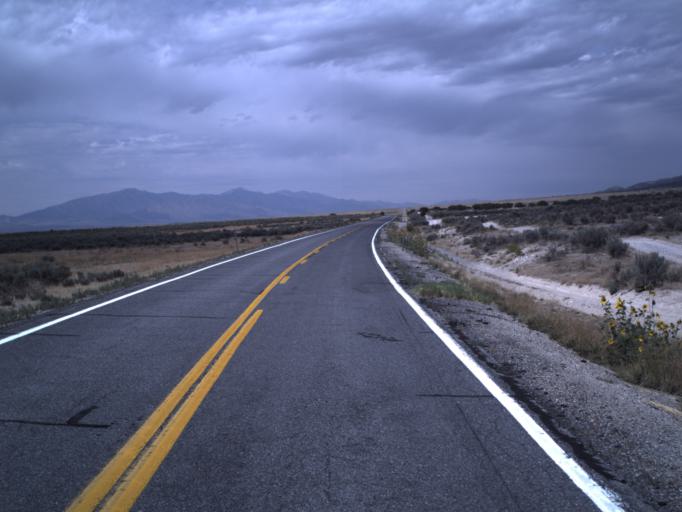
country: US
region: Utah
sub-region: Utah County
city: Eagle Mountain
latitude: 40.2347
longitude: -112.1970
